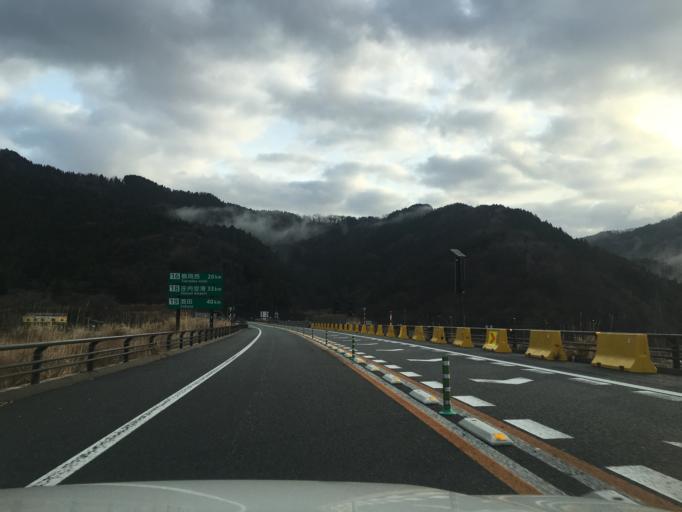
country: JP
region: Yamagata
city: Tsuruoka
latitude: 38.6040
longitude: 139.5850
